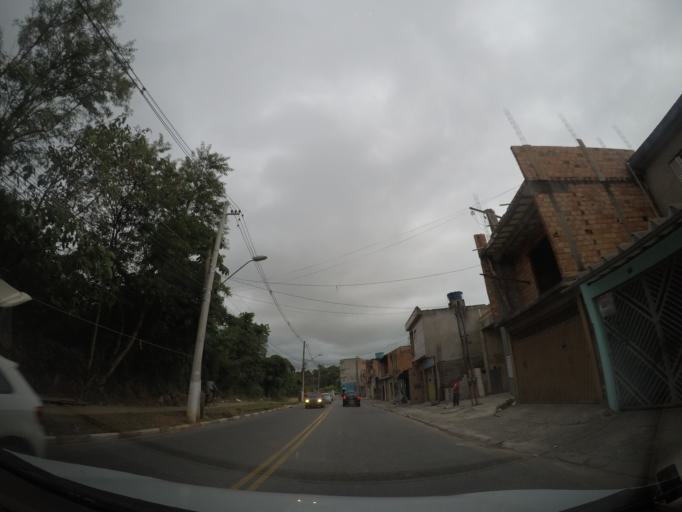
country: BR
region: Sao Paulo
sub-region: Aruja
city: Aruja
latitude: -23.3981
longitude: -46.4269
